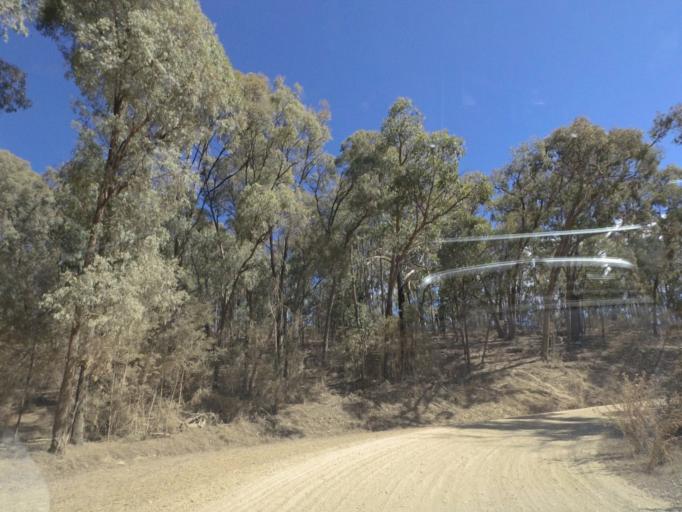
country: AU
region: Victoria
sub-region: Murrindindi
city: Alexandra
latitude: -37.3249
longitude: 145.8067
